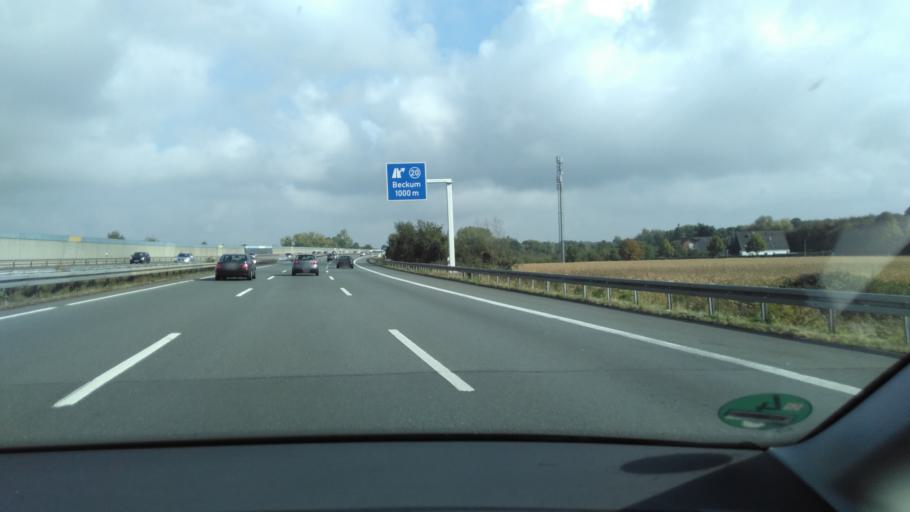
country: DE
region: North Rhine-Westphalia
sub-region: Regierungsbezirk Munster
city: Beckum
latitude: 51.7733
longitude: 8.0125
